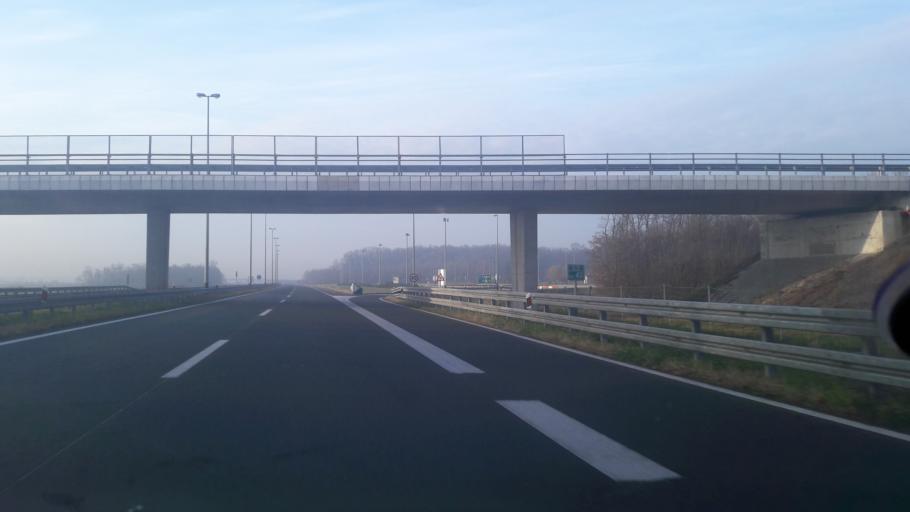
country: HR
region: Osjecko-Baranjska
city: Vuka
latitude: 45.4725
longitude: 18.4823
